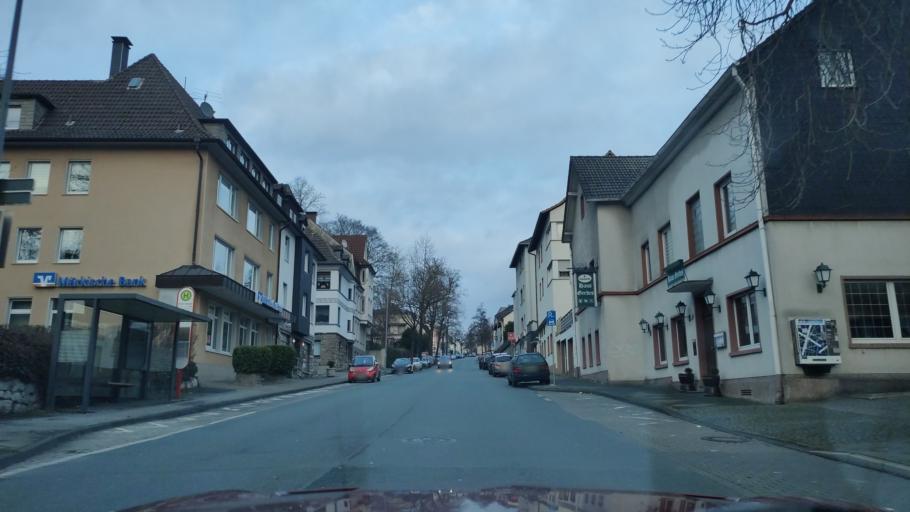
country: DE
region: North Rhine-Westphalia
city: Iserlohn
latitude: 51.3671
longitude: 7.6665
